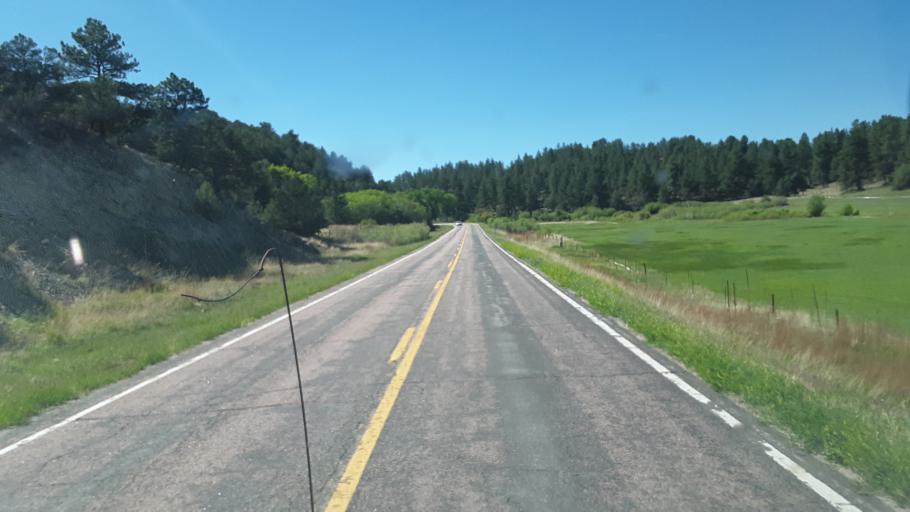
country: US
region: Colorado
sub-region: Custer County
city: Westcliffe
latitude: 38.2412
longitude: -105.5659
